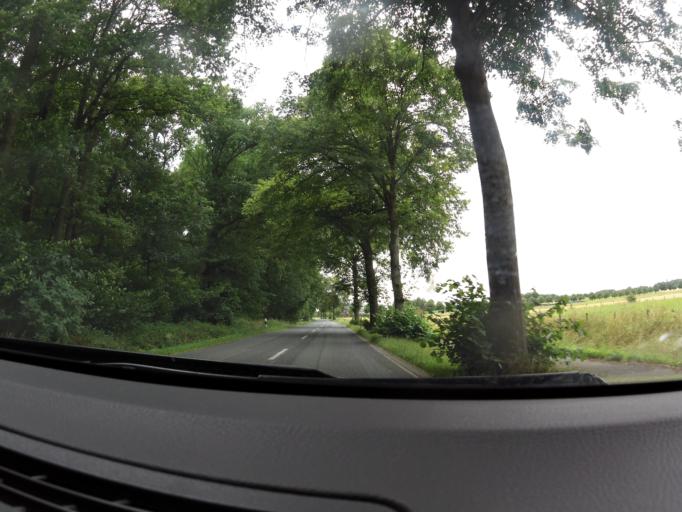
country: DE
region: North Rhine-Westphalia
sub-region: Regierungsbezirk Dusseldorf
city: Sonsbeck
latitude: 51.6130
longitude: 6.4029
